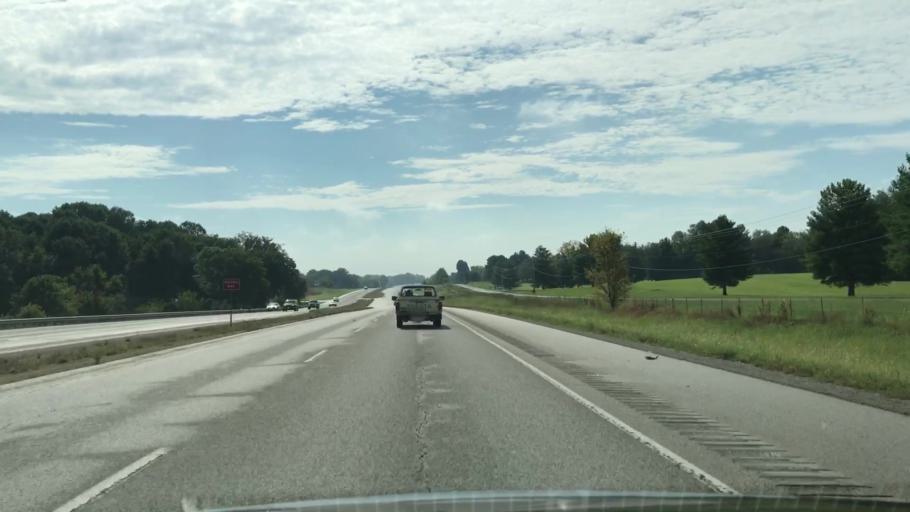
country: US
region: Kentucky
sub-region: Warren County
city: Plano
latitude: 36.8897
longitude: -86.3722
